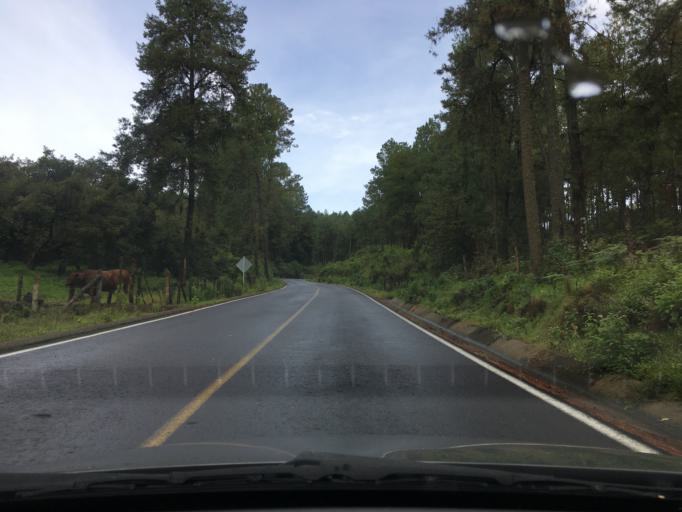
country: MX
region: Michoacan
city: Nuevo San Juan Parangaricutiro
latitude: 19.4453
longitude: -102.1704
